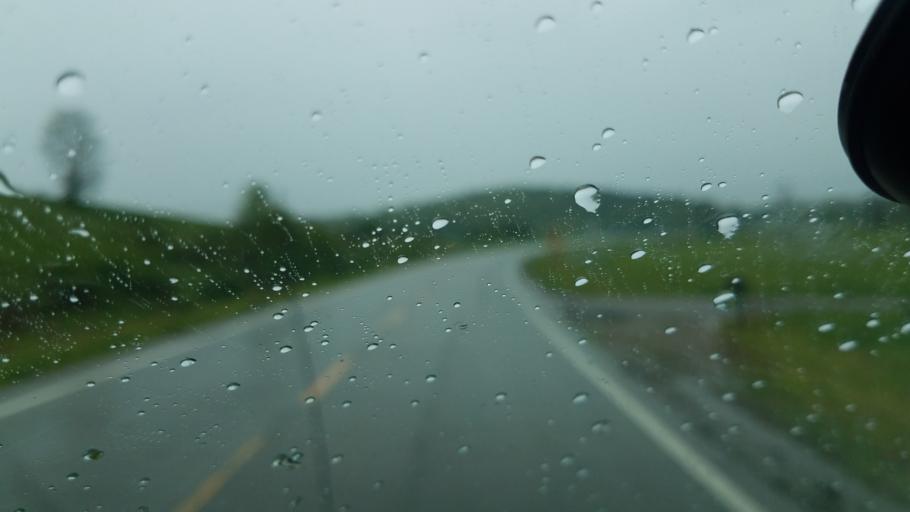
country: US
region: Ohio
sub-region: Muskingum County
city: Frazeysburg
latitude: 40.0871
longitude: -82.0648
